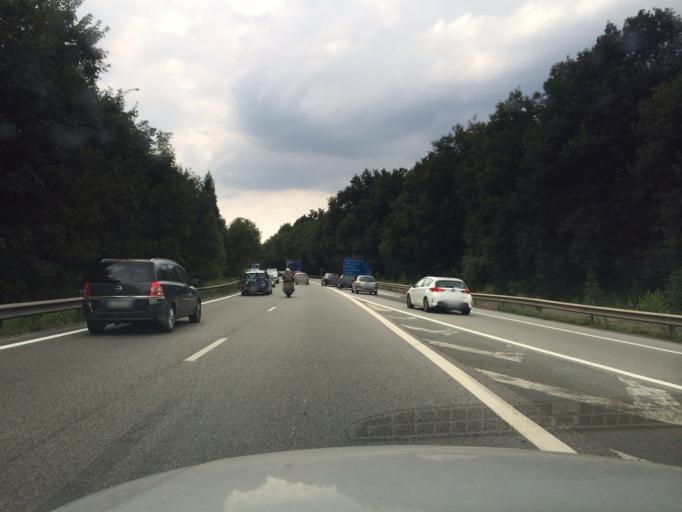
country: FR
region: Ile-de-France
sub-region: Departement des Yvelines
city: Rocquencourt
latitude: 48.8440
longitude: 2.0905
